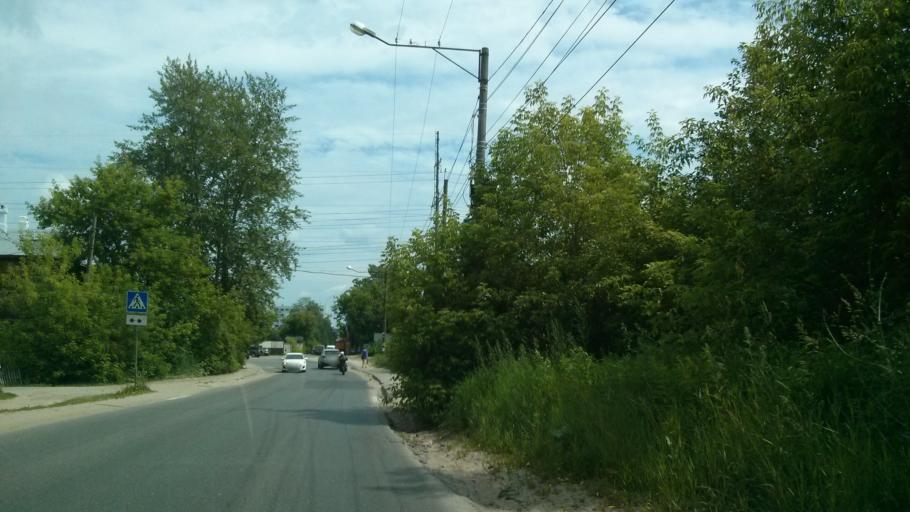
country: RU
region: Nizjnij Novgorod
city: Nizhniy Novgorod
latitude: 56.2996
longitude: 44.0091
